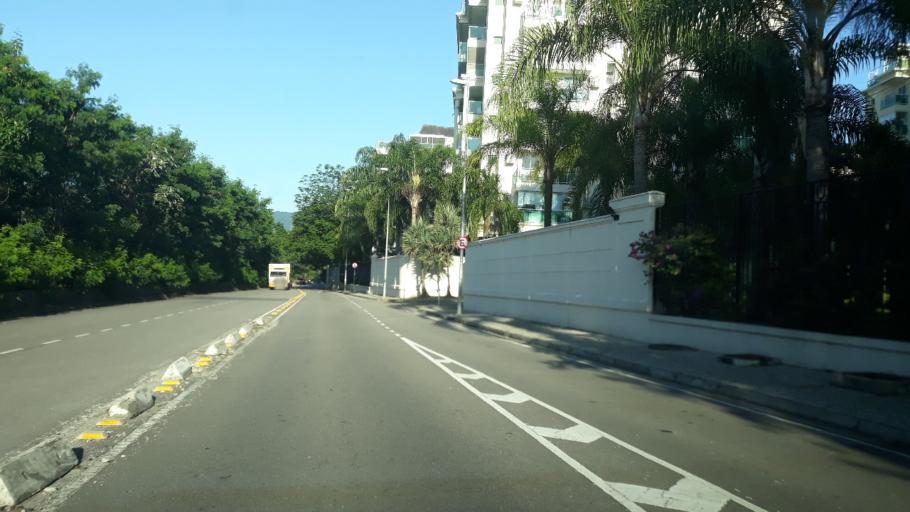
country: BR
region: Rio de Janeiro
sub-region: Rio De Janeiro
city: Rio de Janeiro
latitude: -22.9968
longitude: -43.3489
